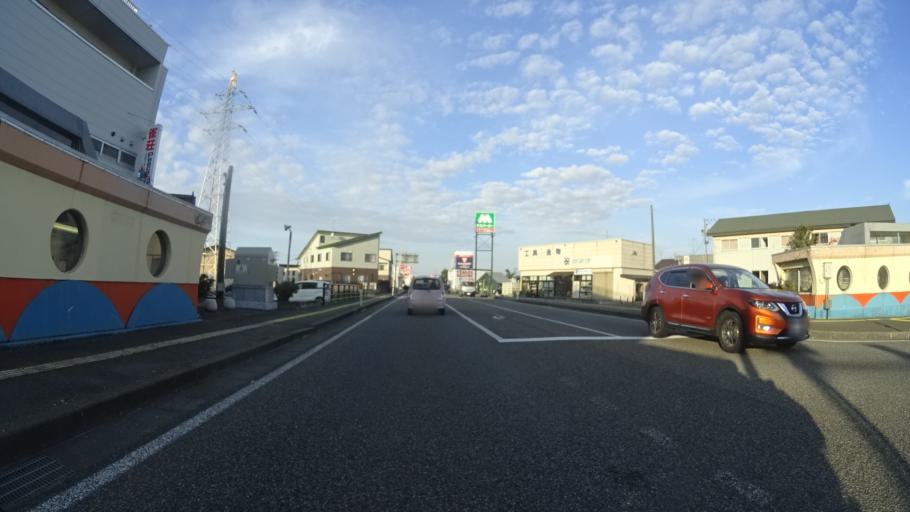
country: JP
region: Niigata
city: Kashiwazaki
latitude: 37.3726
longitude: 138.5786
